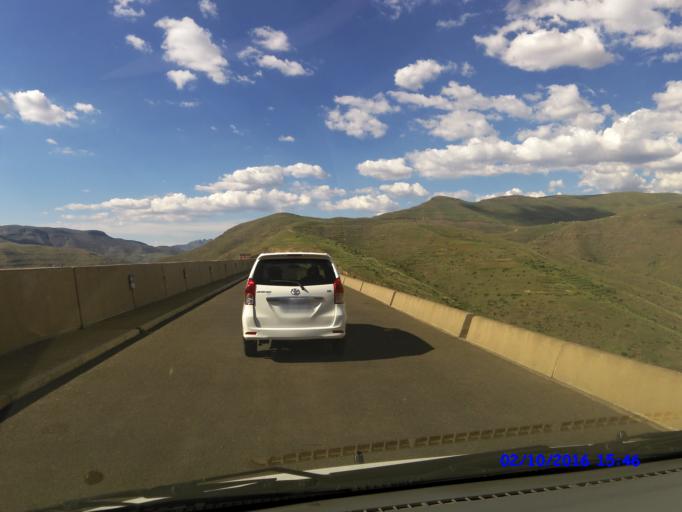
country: LS
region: Maseru
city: Nako
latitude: -29.4604
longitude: 28.0955
